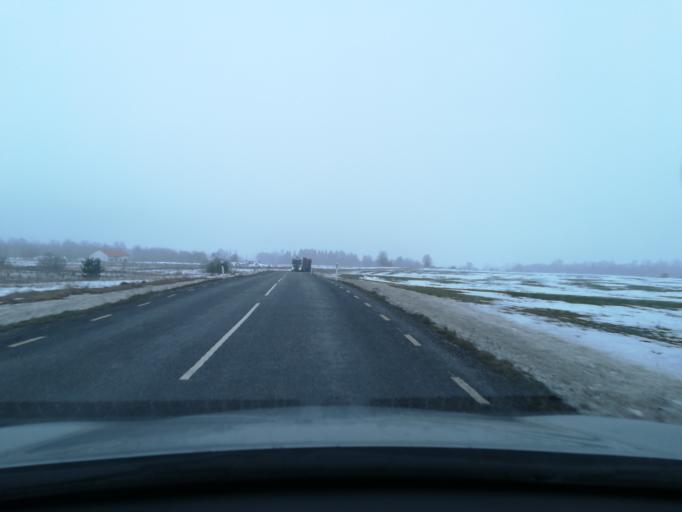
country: EE
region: Harju
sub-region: Raasiku vald
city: Raasiku
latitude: 59.3515
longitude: 25.1323
